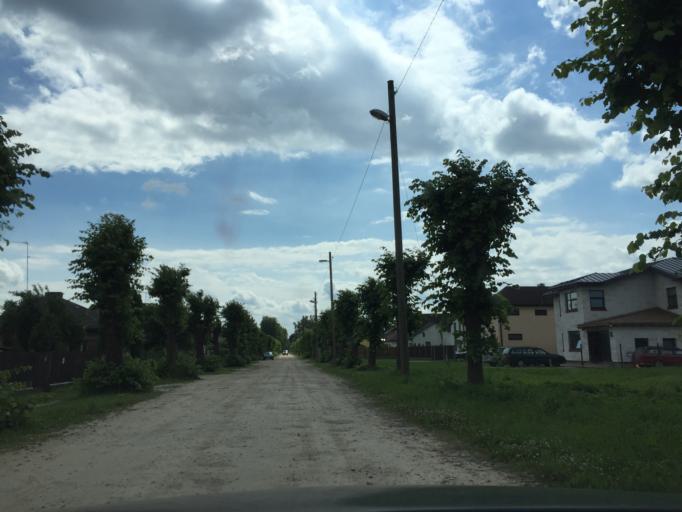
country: LV
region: Jelgava
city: Jelgava
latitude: 56.6513
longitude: 23.6798
